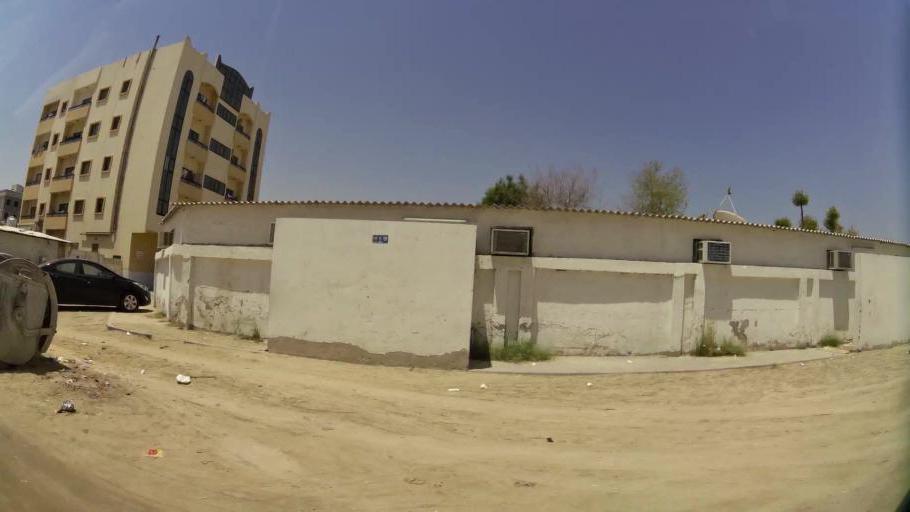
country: AE
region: Ajman
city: Ajman
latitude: 25.3979
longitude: 55.4474
